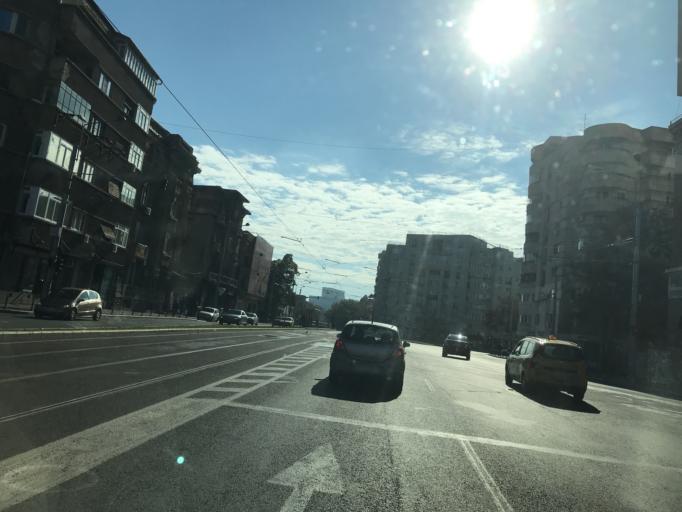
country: RO
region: Bucuresti
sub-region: Municipiul Bucuresti
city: Bucuresti
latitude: 44.4415
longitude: 26.0809
